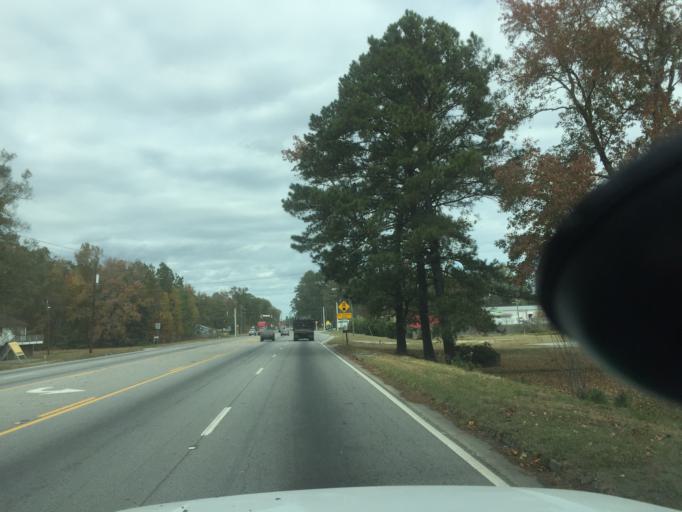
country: US
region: Georgia
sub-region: Chatham County
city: Garden City
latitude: 32.0948
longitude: -81.1965
